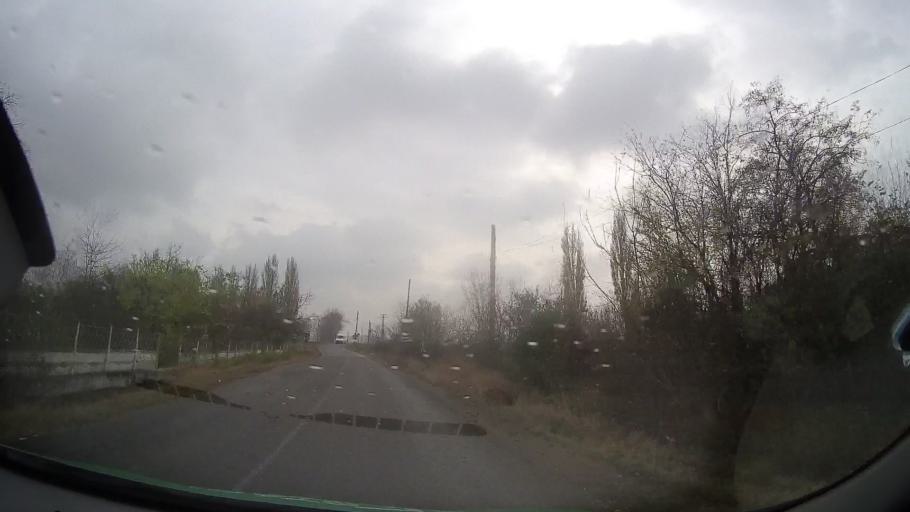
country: RO
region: Prahova
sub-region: Comuna Draganesti
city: Draganesti
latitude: 44.8379
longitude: 26.2690
